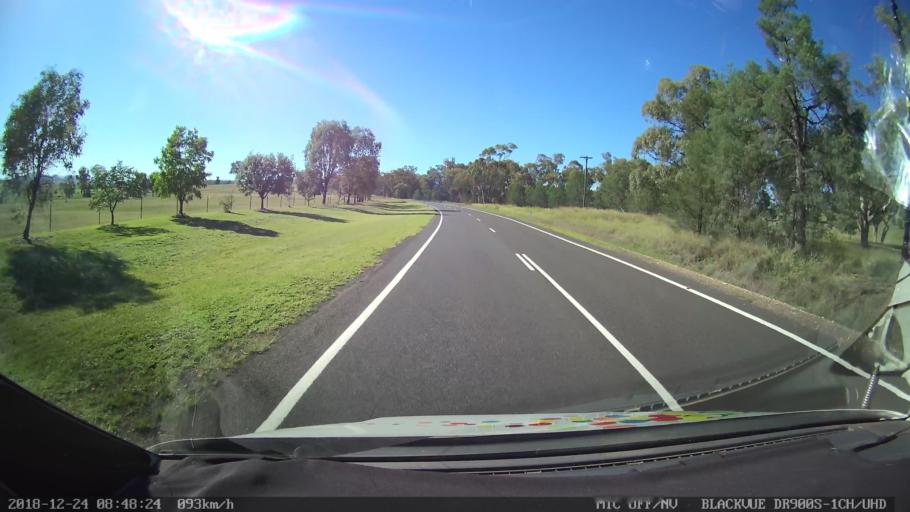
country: AU
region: New South Wales
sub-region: Liverpool Plains
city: Quirindi
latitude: -31.4553
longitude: 150.6461
